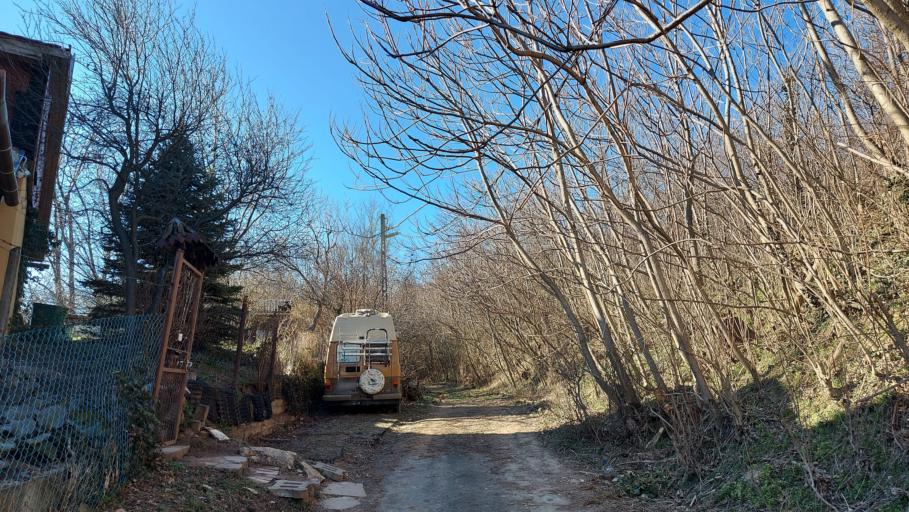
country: HU
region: Pest
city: Budaors
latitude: 47.4750
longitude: 18.9681
